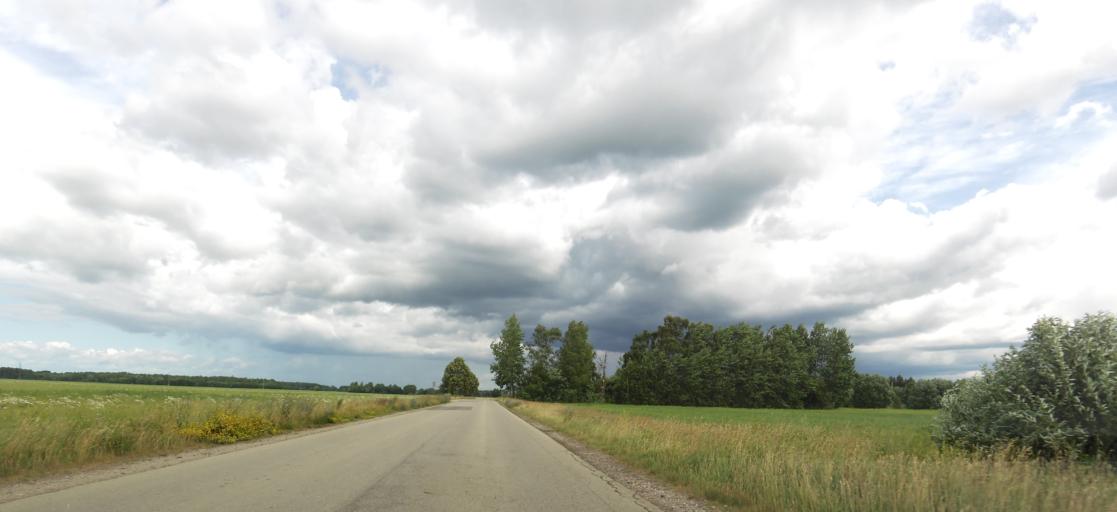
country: LT
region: Panevezys
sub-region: Birzai
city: Birzai
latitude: 56.3253
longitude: 24.8074
